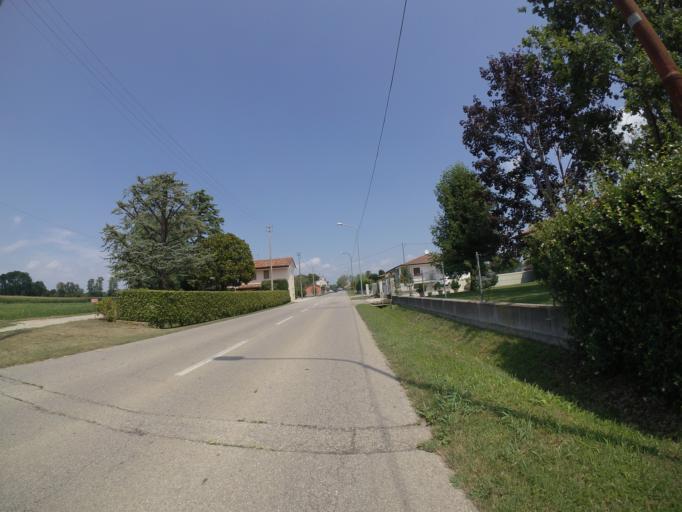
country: IT
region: Friuli Venezia Giulia
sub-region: Provincia di Udine
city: Sedegliano
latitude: 45.9923
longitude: 12.9689
